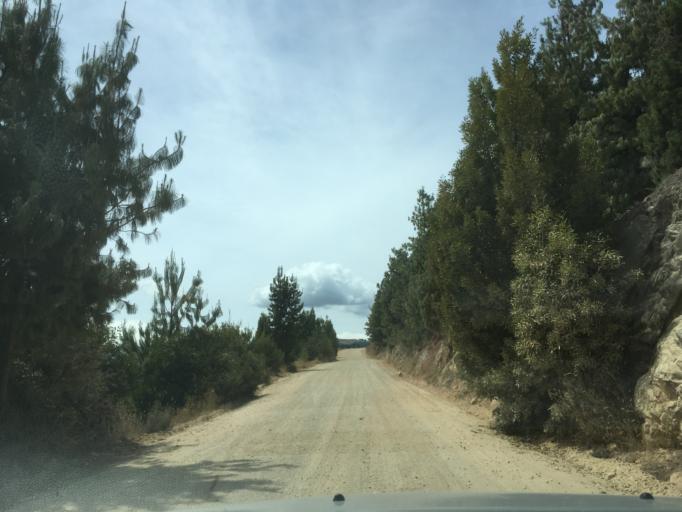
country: CO
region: Boyaca
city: Aquitania
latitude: 5.5750
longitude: -72.9347
